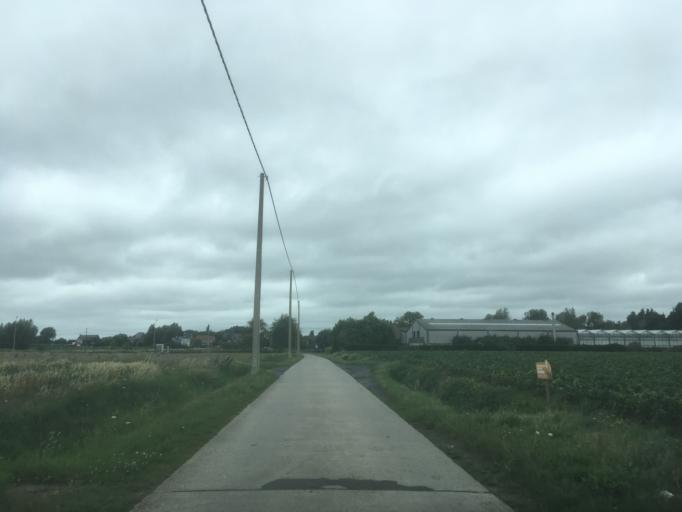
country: BE
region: Flanders
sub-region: Provincie West-Vlaanderen
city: Roeselare
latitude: 50.9266
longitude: 3.0925
